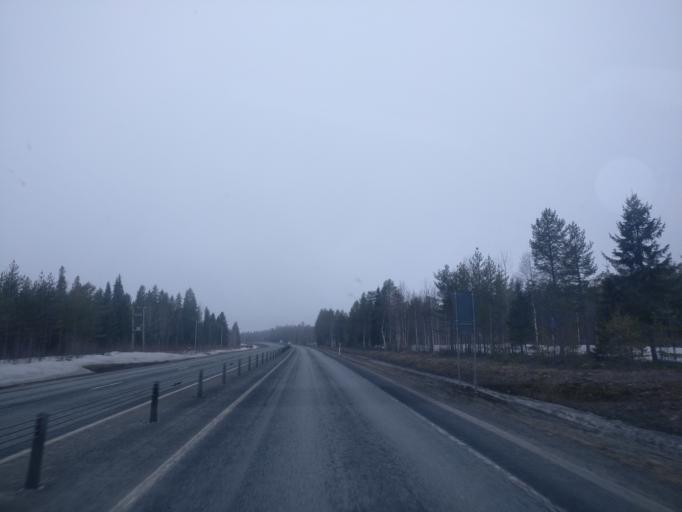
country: FI
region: Lapland
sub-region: Kemi-Tornio
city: Simo
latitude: 65.6675
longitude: 24.9740
